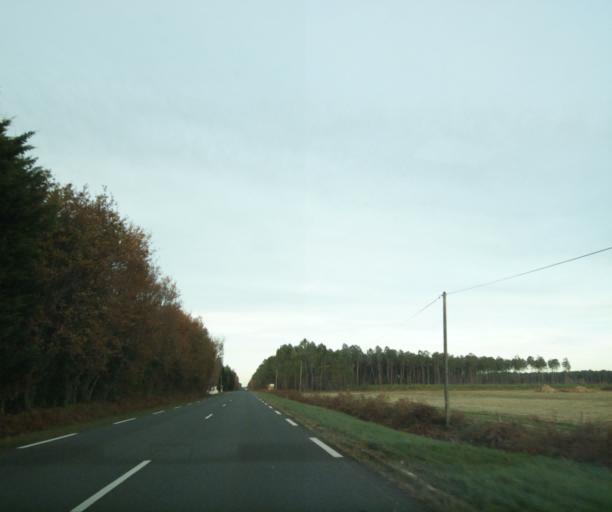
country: FR
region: Aquitaine
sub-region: Departement de la Gironde
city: Bazas
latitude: 44.3204
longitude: -0.2440
